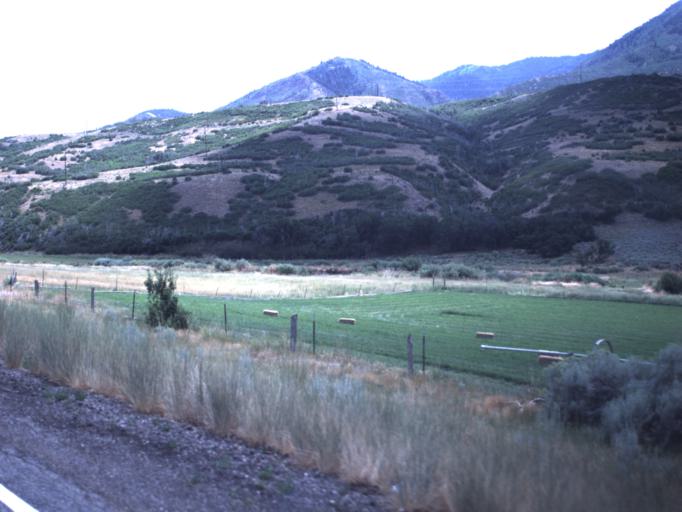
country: US
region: Utah
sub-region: Juab County
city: Nephi
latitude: 39.7161
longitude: -111.7256
